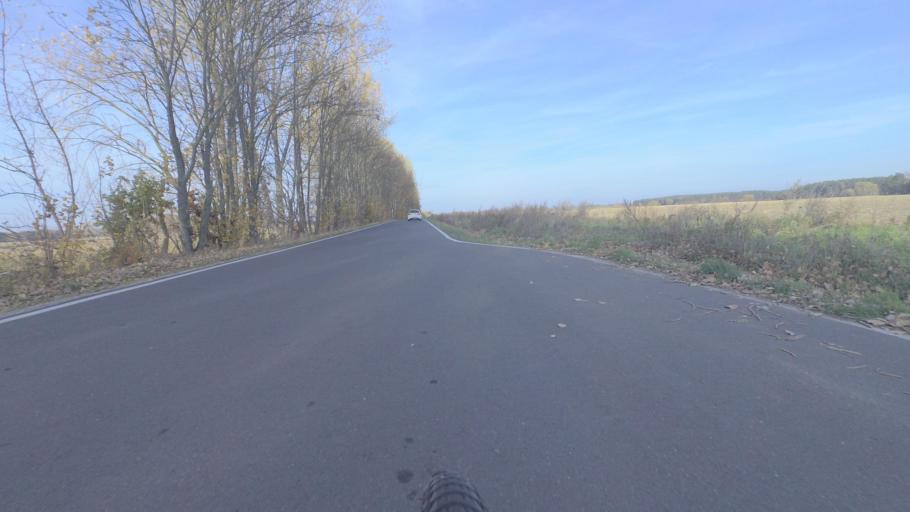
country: DE
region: Brandenburg
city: Ludwigsfelde
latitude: 52.2522
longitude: 13.2984
